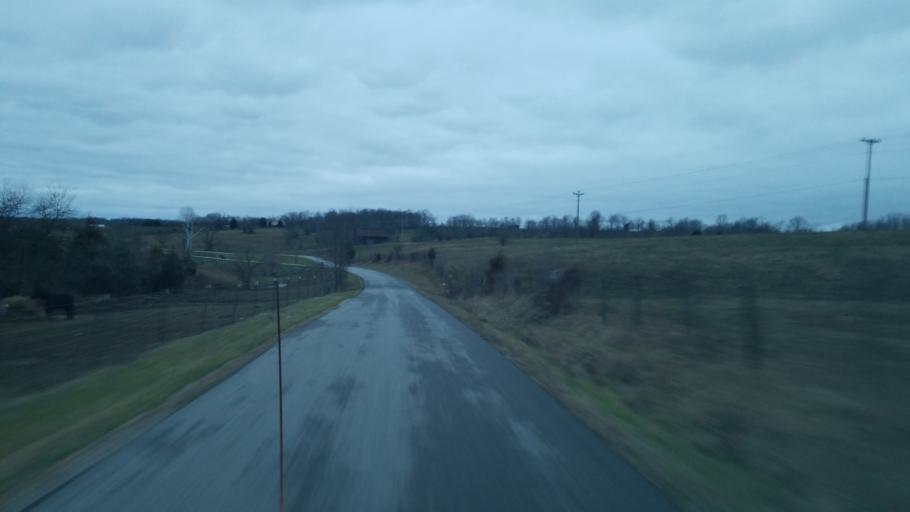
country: US
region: Kentucky
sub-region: Fleming County
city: Flemingsburg
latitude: 38.5046
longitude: -83.6825
